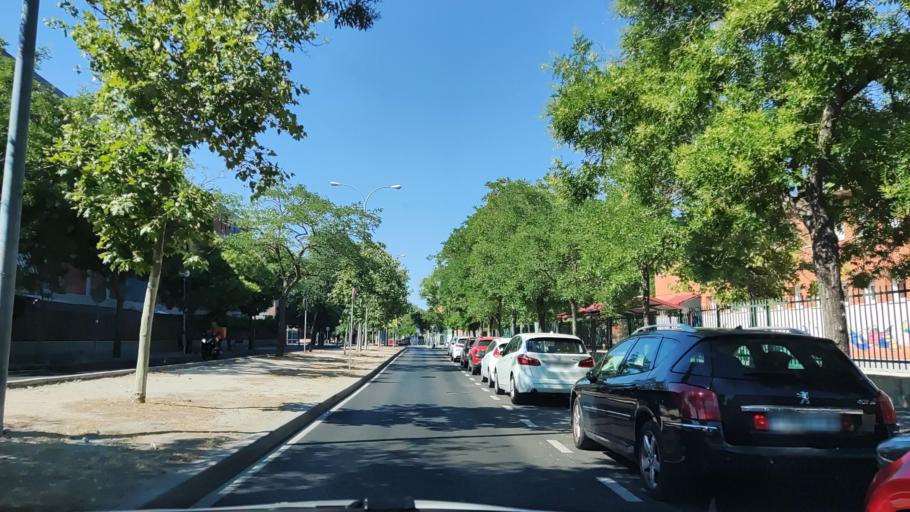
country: ES
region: Madrid
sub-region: Provincia de Madrid
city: Leganes
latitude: 40.3371
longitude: -3.7647
